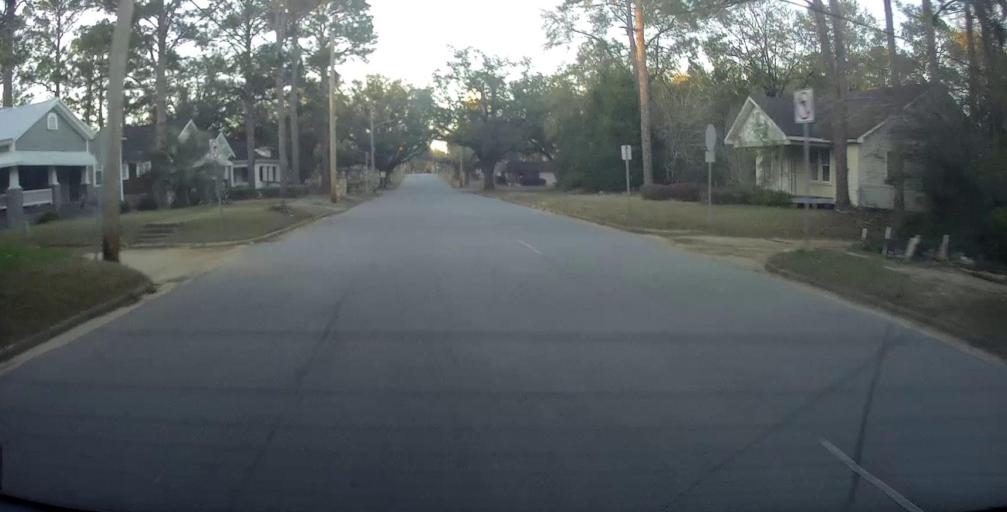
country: US
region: Georgia
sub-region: Dougherty County
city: Albany
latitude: 31.5699
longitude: -84.1619
